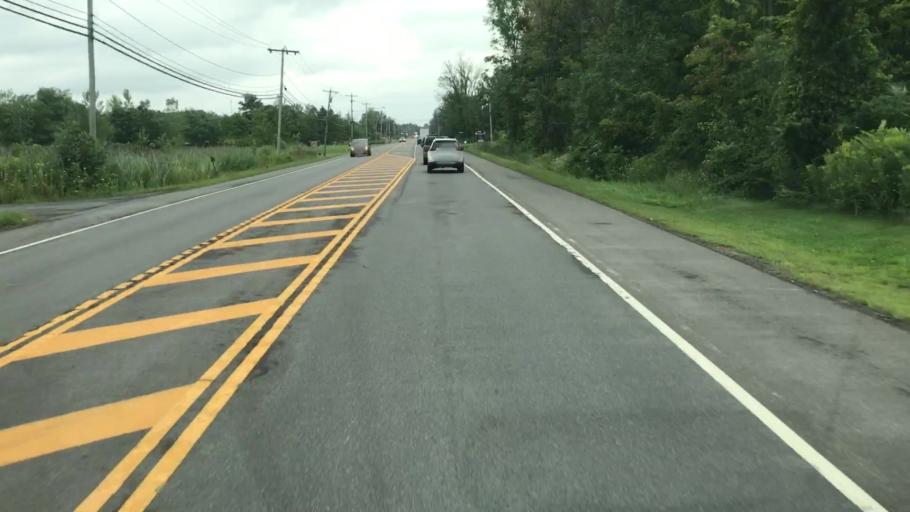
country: US
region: New York
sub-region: Onondaga County
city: Liverpool
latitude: 43.1863
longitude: -76.2104
